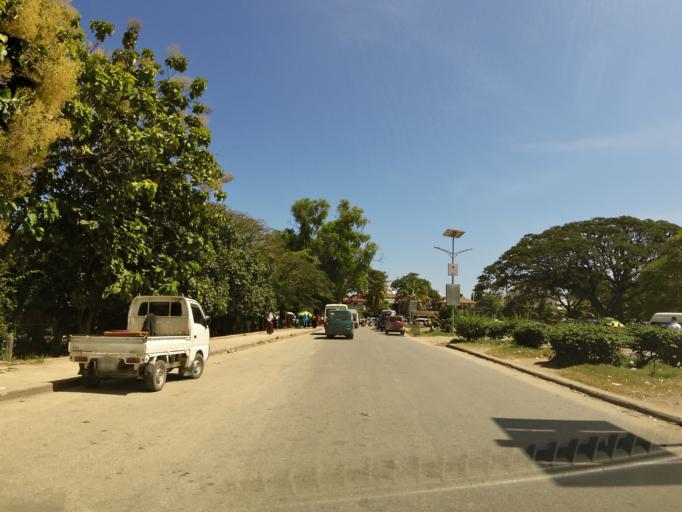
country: TZ
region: Zanzibar Urban/West
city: Zanzibar
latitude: -6.1646
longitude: 39.1941
